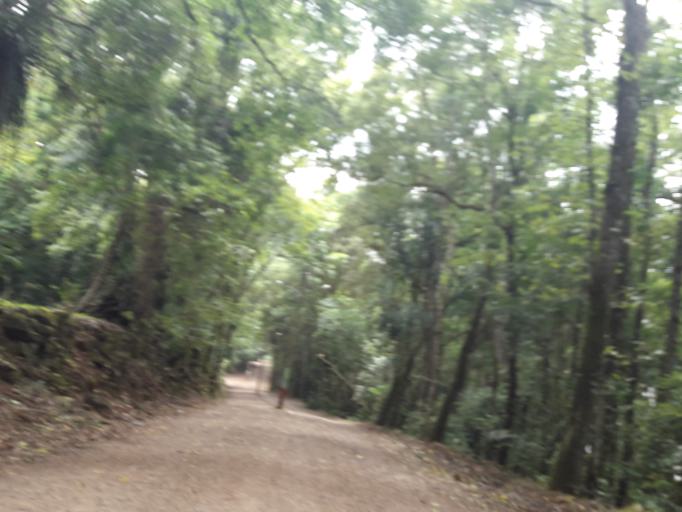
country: BR
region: Rio Grande do Sul
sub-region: Frederico Westphalen
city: Frederico Westphalen
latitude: -27.0893
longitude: -53.3794
